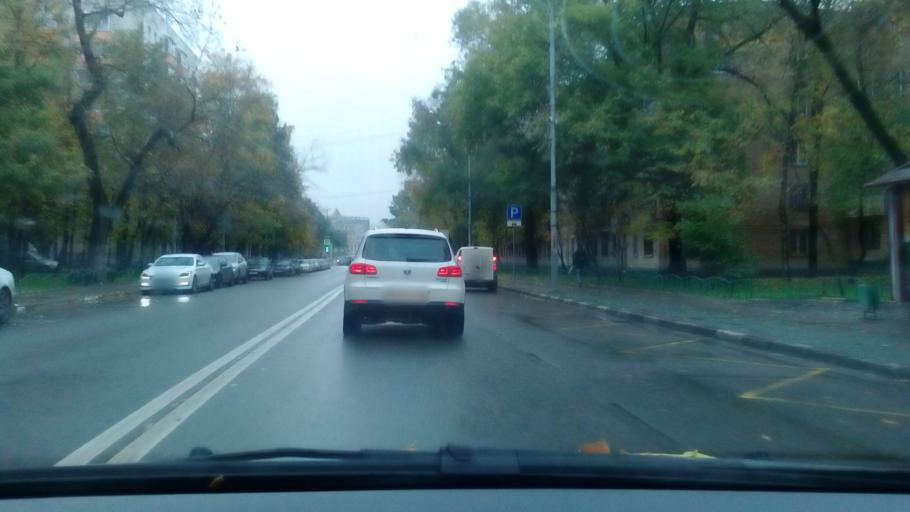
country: RU
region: Moscow
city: Mar'ina Roshcha
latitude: 55.7963
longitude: 37.5764
